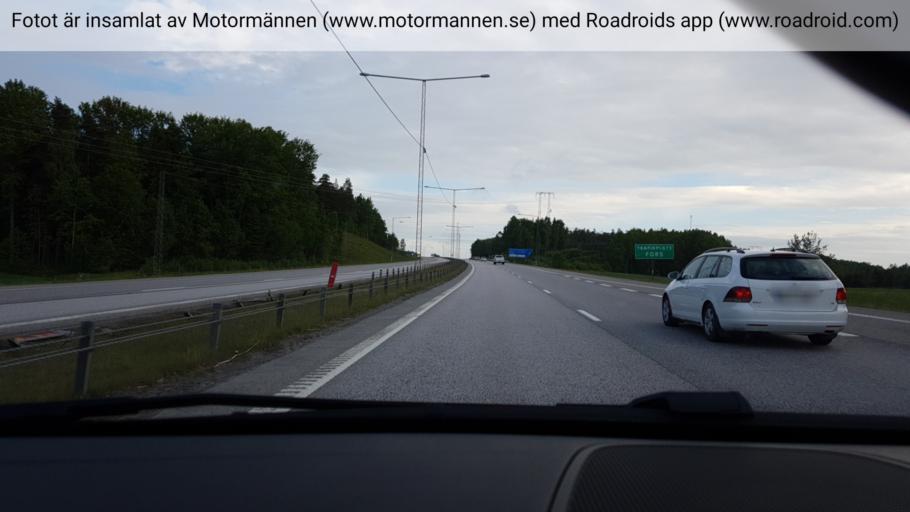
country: SE
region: Stockholm
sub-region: Haninge Kommun
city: Jordbro
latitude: 59.1171
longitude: 18.1286
